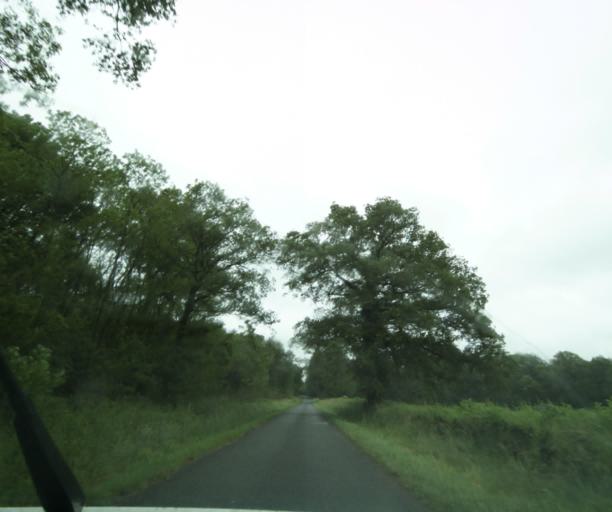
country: FR
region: Bourgogne
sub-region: Departement de Saone-et-Loire
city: Palinges
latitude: 46.5251
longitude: 4.2250
